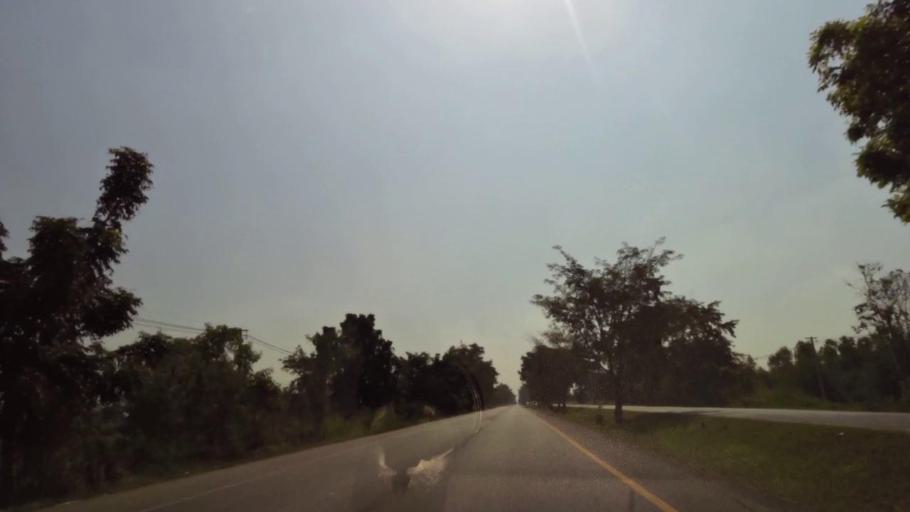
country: TH
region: Phichit
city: Bueng Na Rang
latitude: 16.2866
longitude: 100.1277
